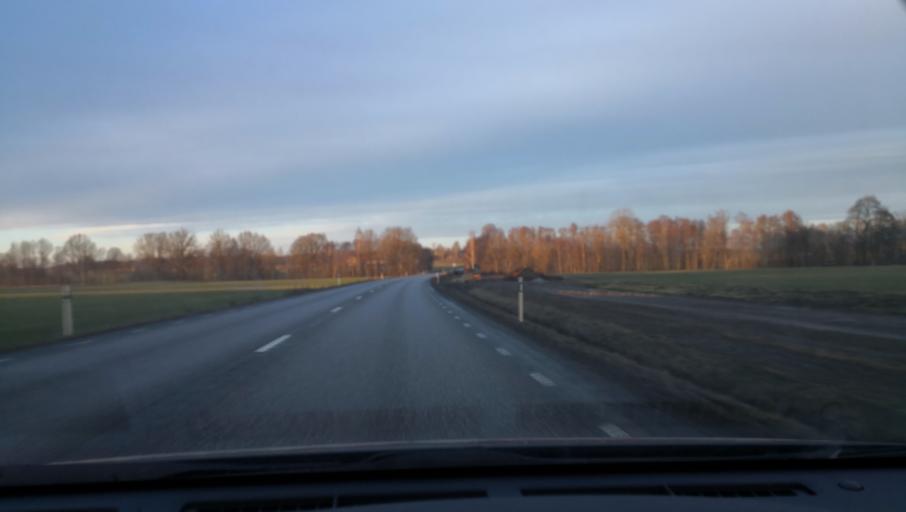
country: SE
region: OErebro
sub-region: Lekebergs Kommun
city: Fjugesta
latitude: 59.2179
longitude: 14.8922
